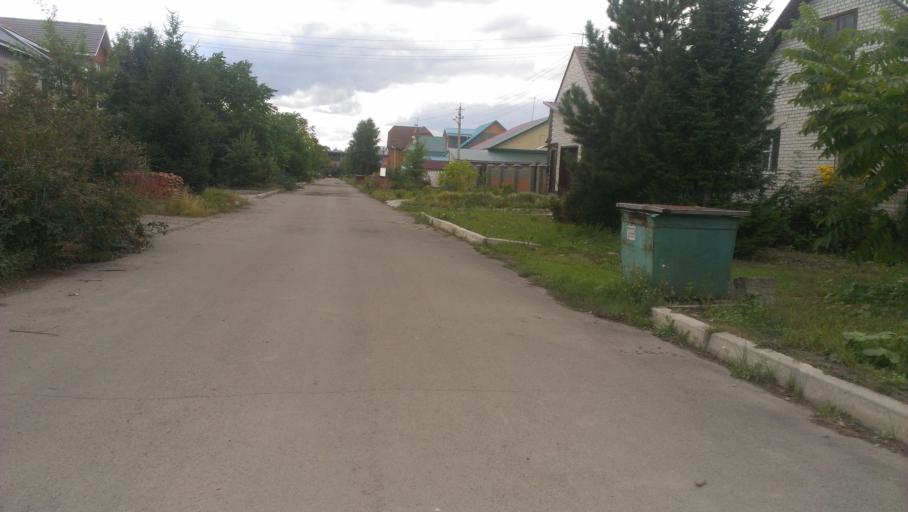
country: RU
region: Altai Krai
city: Novosilikatnyy
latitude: 53.3519
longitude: 83.6481
